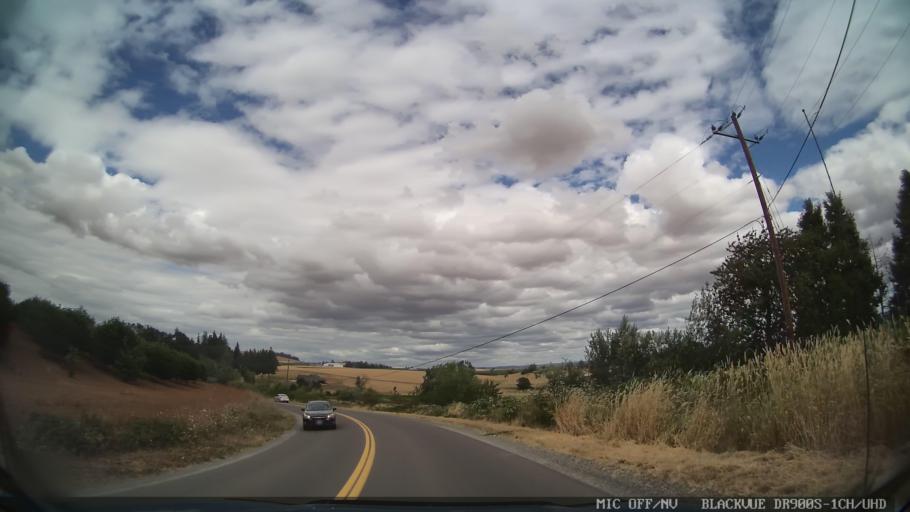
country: US
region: Oregon
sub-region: Marion County
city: Aumsville
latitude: 44.8604
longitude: -122.8523
